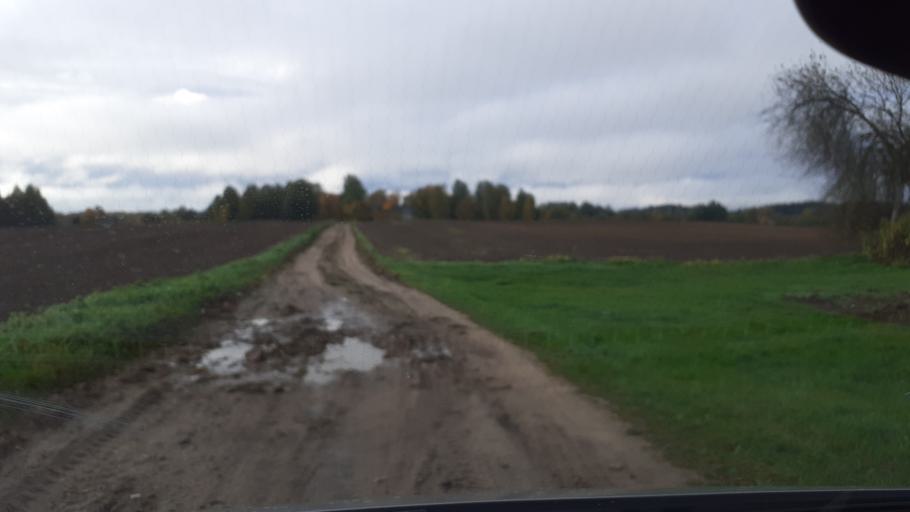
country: LV
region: Kuldigas Rajons
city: Kuldiga
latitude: 56.9766
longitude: 21.9397
